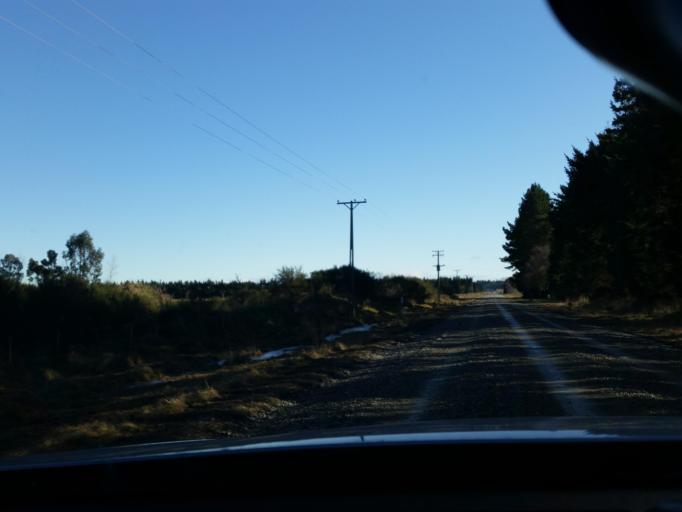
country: NZ
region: Southland
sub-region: Gore District
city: Gore
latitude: -45.8115
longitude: 168.6981
